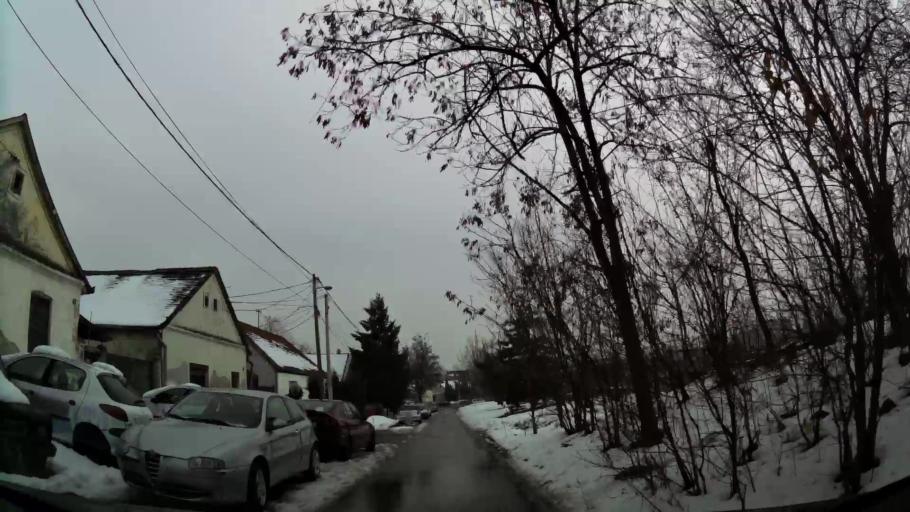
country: RS
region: Central Serbia
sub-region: Belgrade
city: Zemun
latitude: 44.8500
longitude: 20.3778
